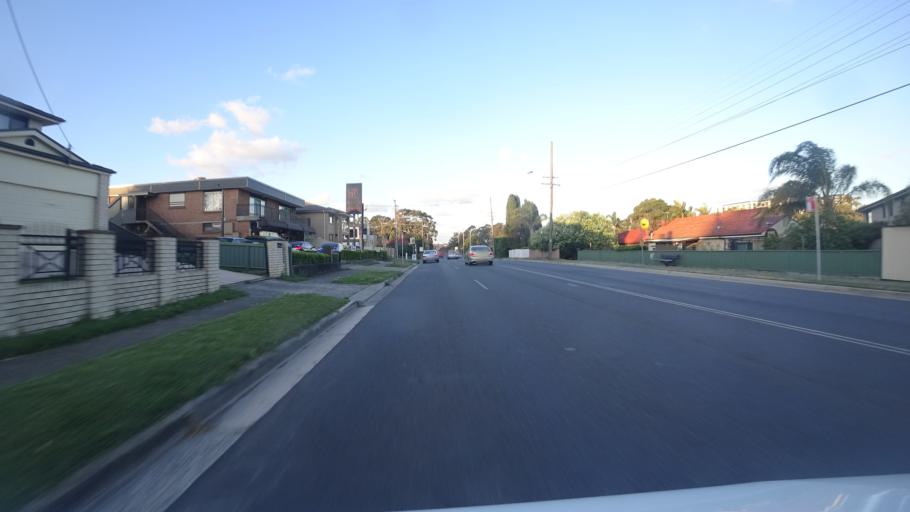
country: AU
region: New South Wales
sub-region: Ryde
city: North Ryde
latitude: -33.7930
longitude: 151.1284
